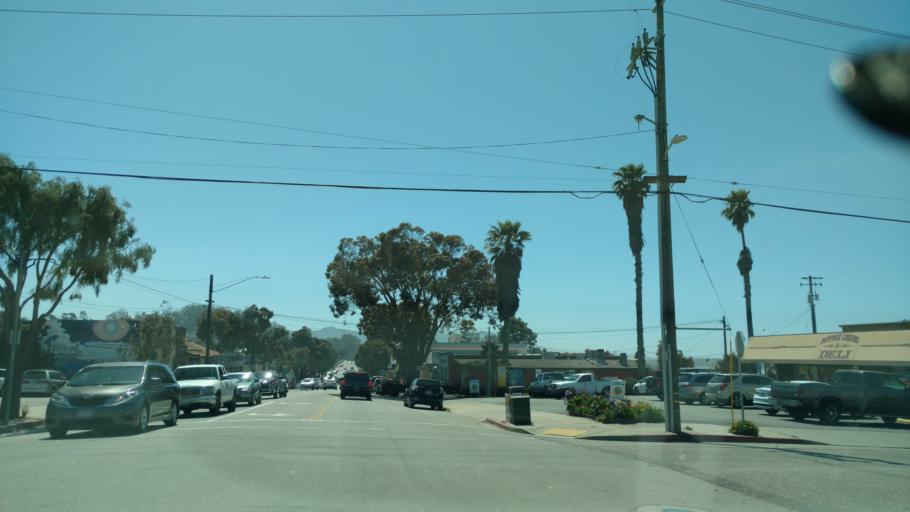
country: US
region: California
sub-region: San Luis Obispo County
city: Morro Bay
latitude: 35.3680
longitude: -120.8501
